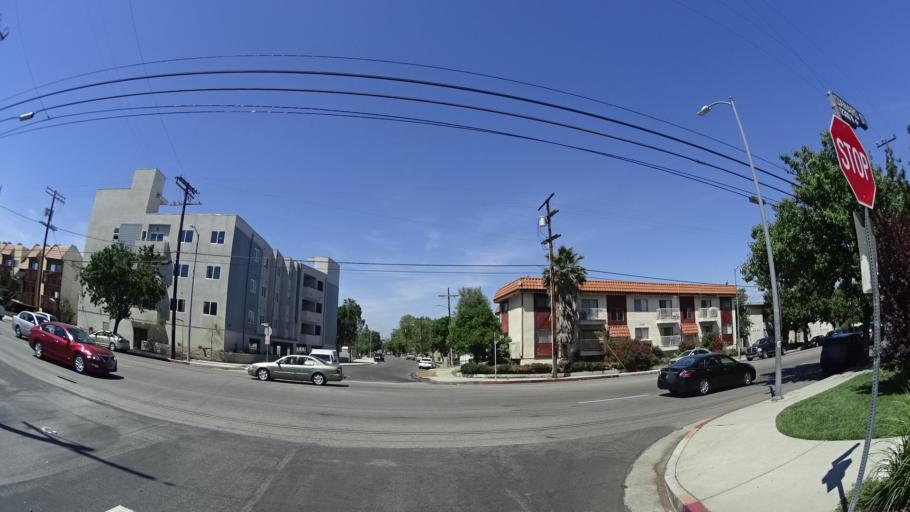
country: US
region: California
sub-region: Los Angeles County
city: North Hollywood
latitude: 34.1792
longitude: -118.4032
